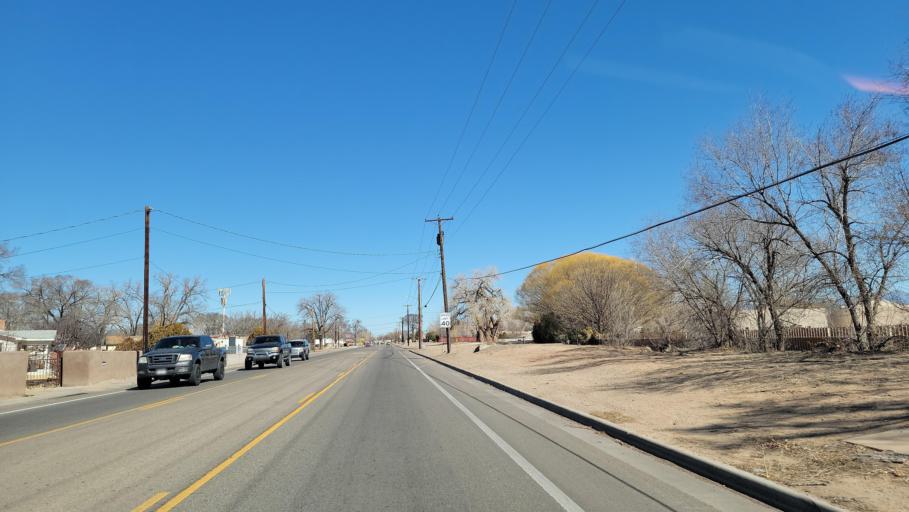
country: US
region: New Mexico
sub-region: Bernalillo County
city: South Valley
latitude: 35.0124
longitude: -106.6868
